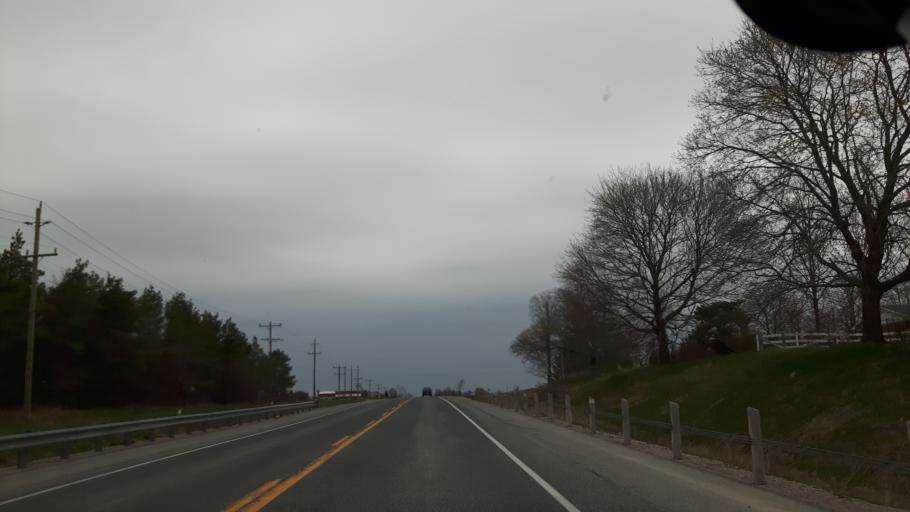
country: CA
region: Ontario
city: Goderich
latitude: 43.6720
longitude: -81.6238
